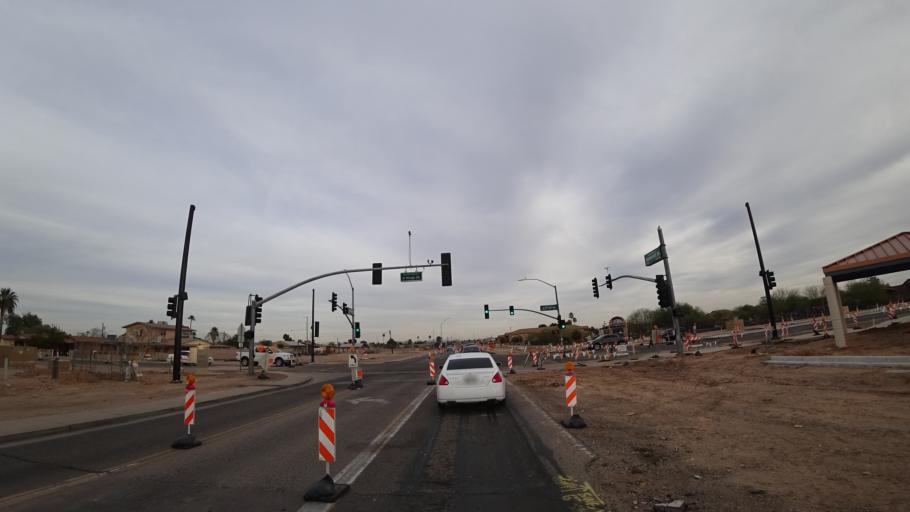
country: US
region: Arizona
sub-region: Maricopa County
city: El Mirage
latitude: 33.6090
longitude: -112.3251
